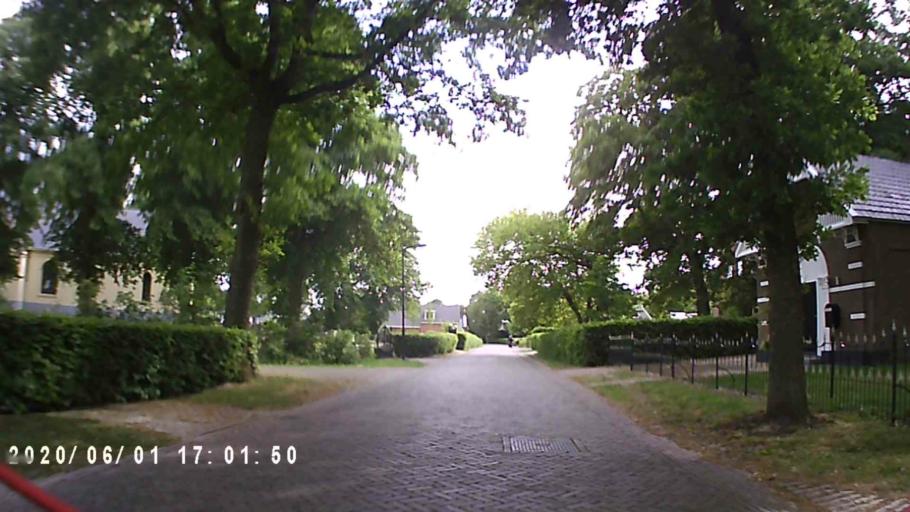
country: NL
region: Friesland
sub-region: Gemeente Tytsjerksteradiel
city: Hurdegaryp
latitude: 53.1795
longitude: 5.9273
